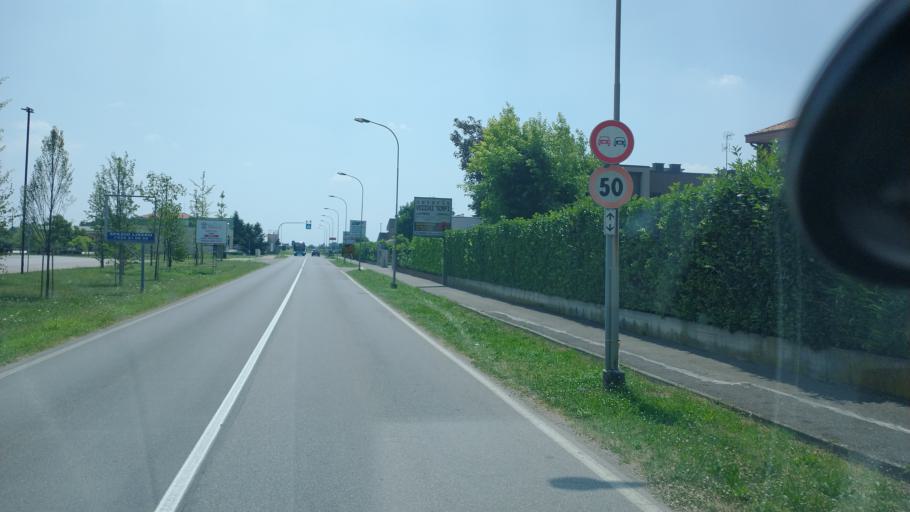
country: IT
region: Lombardy
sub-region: Provincia di Bergamo
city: Calvenzano
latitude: 45.4937
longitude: 9.5962
